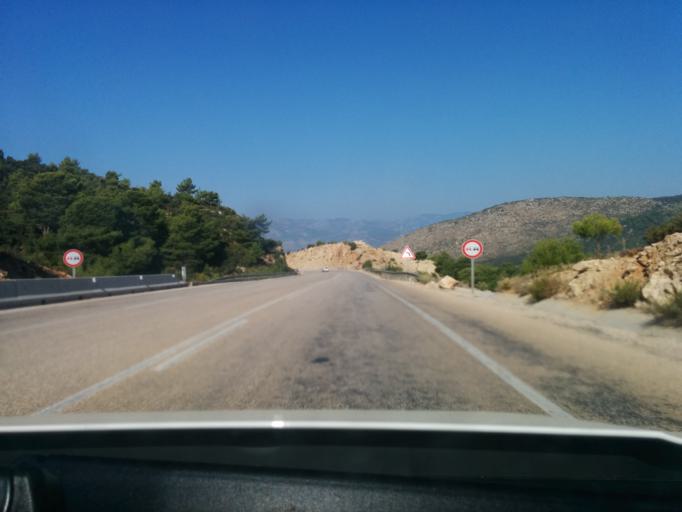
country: TR
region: Antalya
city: Kalkan
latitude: 36.2774
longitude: 29.3907
